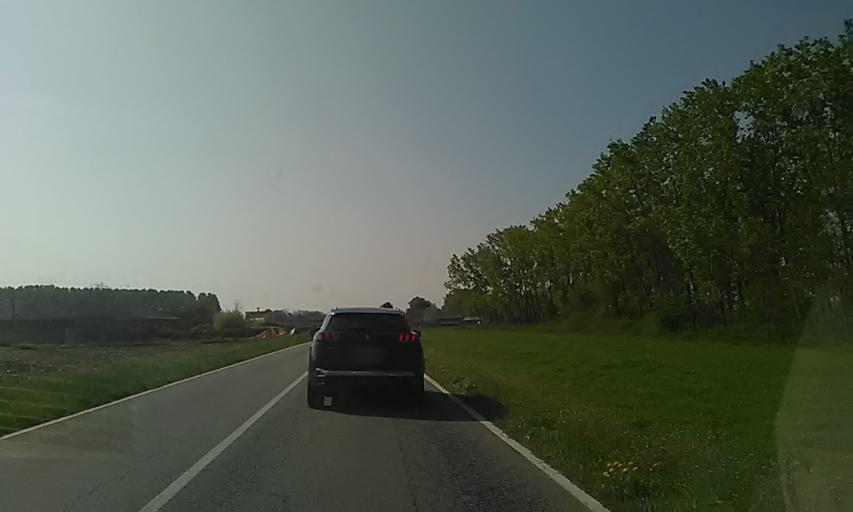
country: IT
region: Piedmont
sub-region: Provincia di Vercelli
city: Ghislarengo
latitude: 45.5185
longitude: 8.3868
